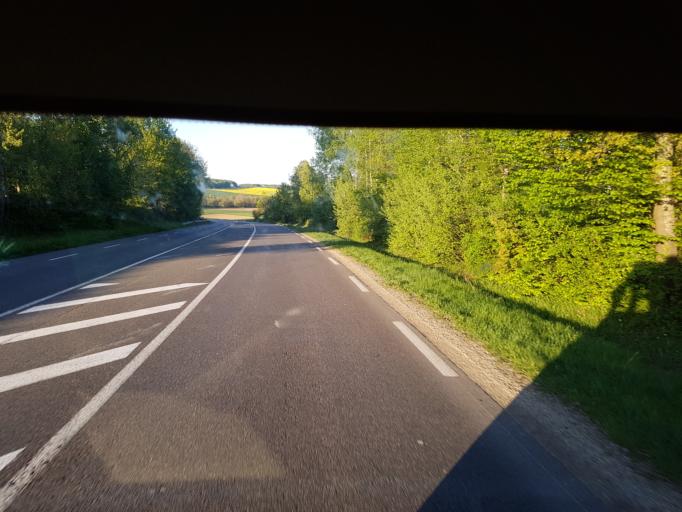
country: FR
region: Champagne-Ardenne
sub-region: Departement de la Marne
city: Esternay
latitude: 48.7197
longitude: 3.5537
